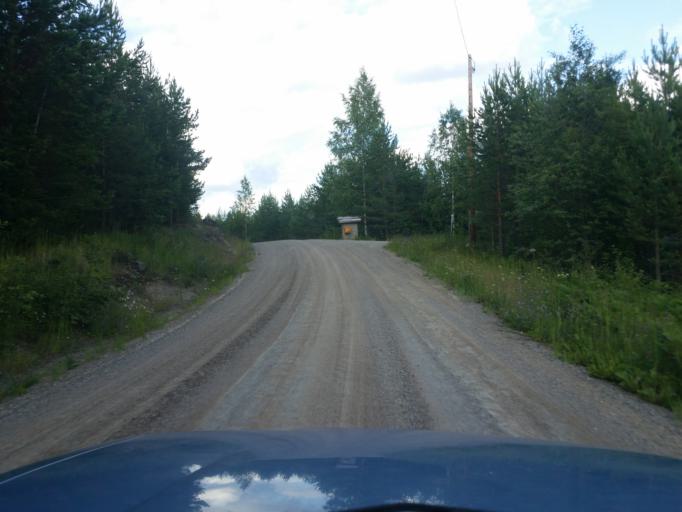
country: FI
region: Southern Savonia
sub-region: Savonlinna
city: Sulkava
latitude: 61.6929
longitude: 28.2913
